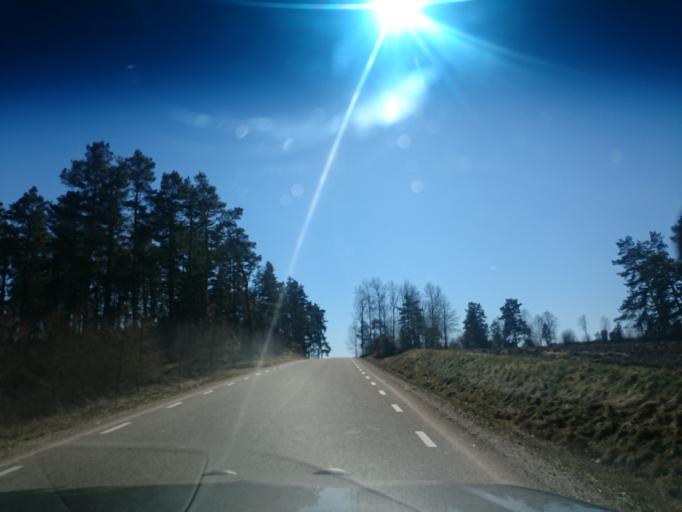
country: SE
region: Joenkoeping
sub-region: Vetlanda Kommun
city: Landsbro
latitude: 57.2237
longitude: 14.9560
